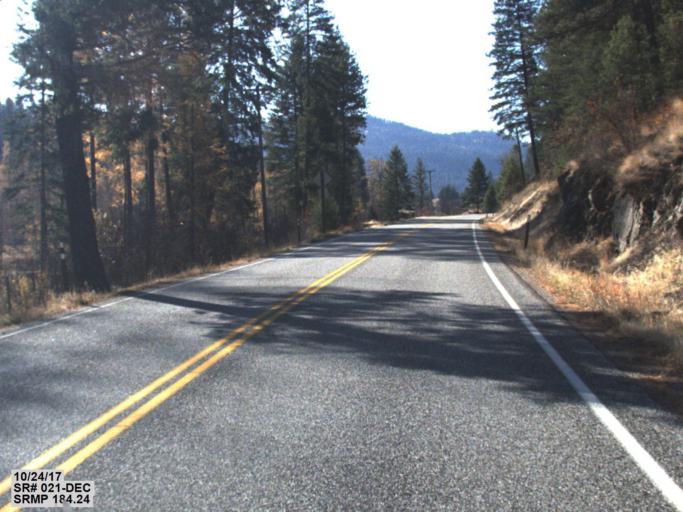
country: CA
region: British Columbia
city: Grand Forks
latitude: 48.9177
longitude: -118.5658
